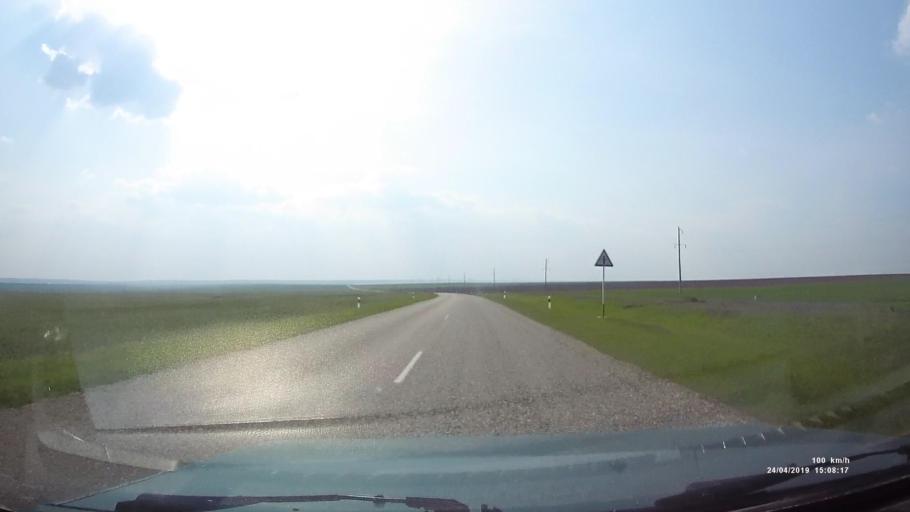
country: RU
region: Rostov
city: Remontnoye
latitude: 46.5600
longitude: 43.3863
